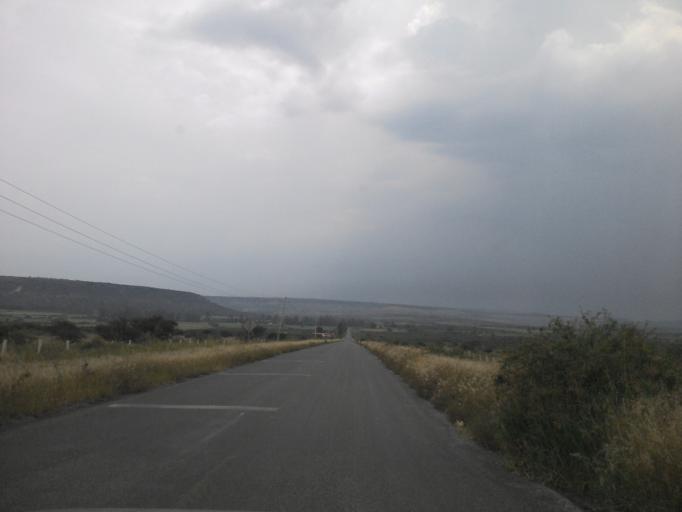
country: MX
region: Jalisco
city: San Diego de Alejandria
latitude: 20.9041
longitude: -102.0482
